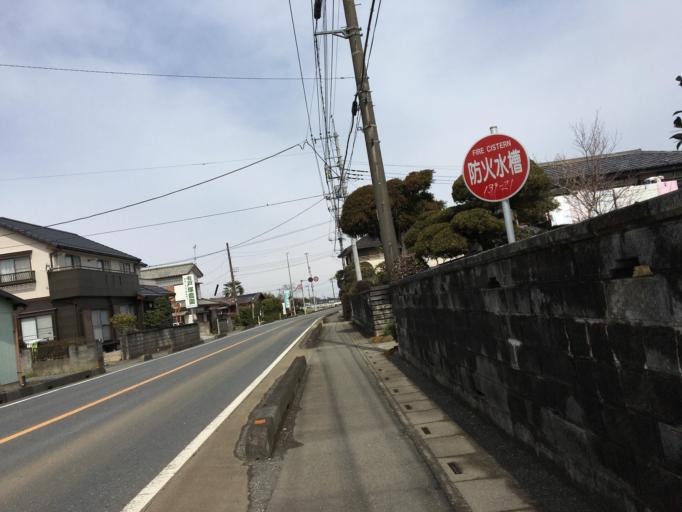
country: JP
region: Saitama
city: Yorii
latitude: 36.1383
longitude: 139.2126
